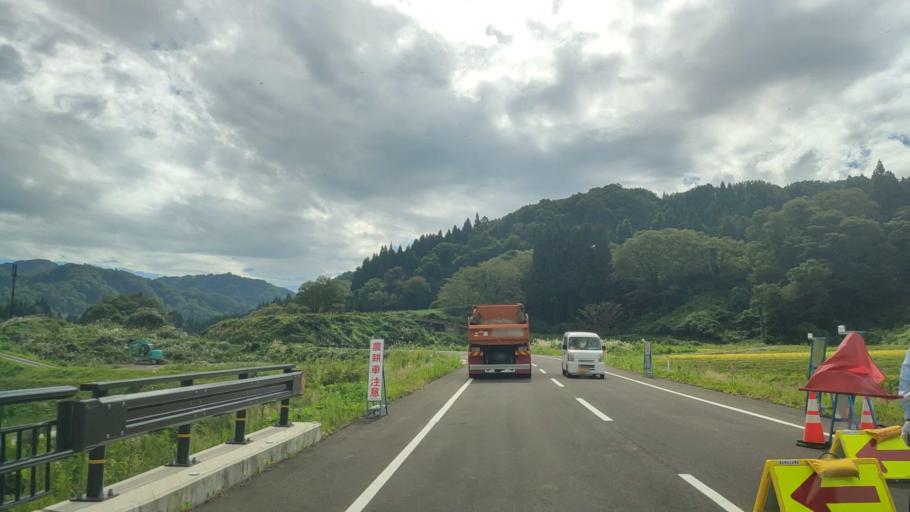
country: JP
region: Niigata
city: Arai
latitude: 36.9499
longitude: 138.2812
